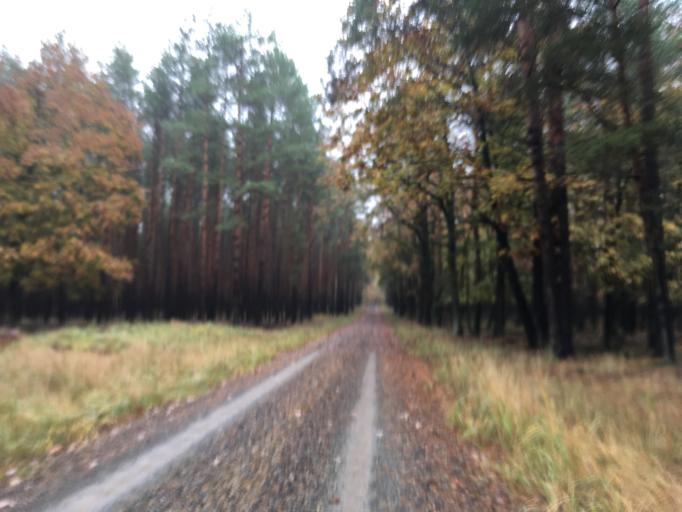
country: DE
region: Brandenburg
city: Beeskow
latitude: 52.2327
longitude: 14.2866
